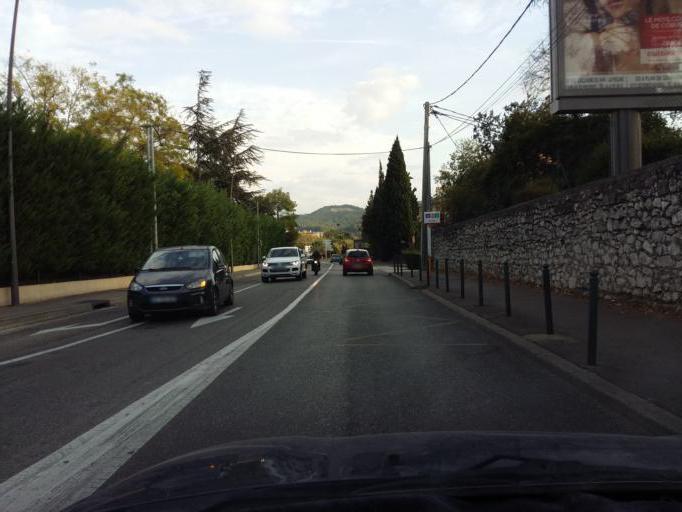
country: FR
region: Provence-Alpes-Cote d'Azur
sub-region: Departement des Bouches-du-Rhone
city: Aix-en-Provence
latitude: 43.5175
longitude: 5.4651
